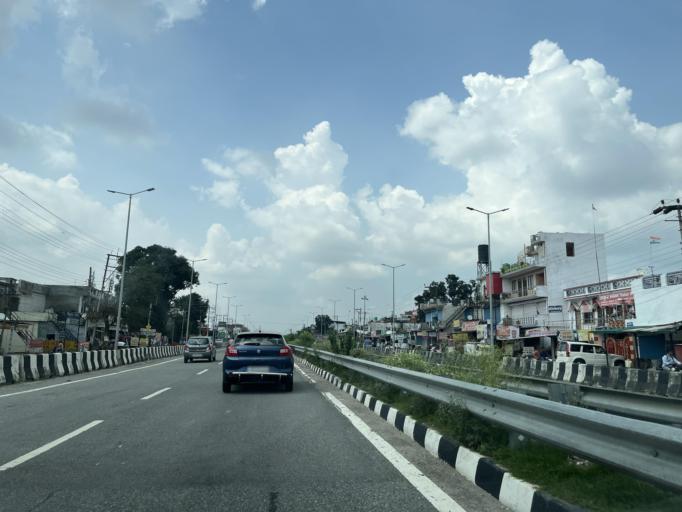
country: IN
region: Uttarakhand
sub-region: Dehradun
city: Raipur
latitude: 30.2562
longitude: 78.0921
